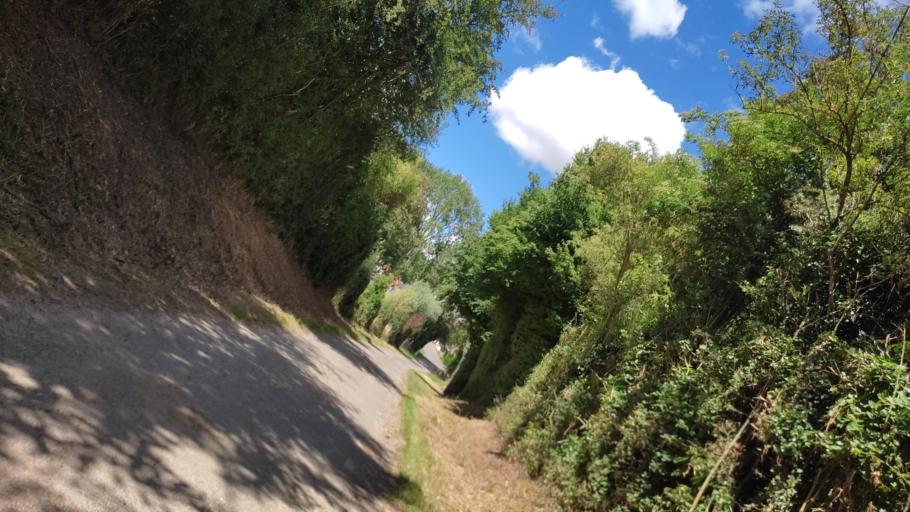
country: FR
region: Nord-Pas-de-Calais
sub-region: Departement du Pas-de-Calais
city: Beaumetz-les-Loges
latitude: 50.2235
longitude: 2.6462
